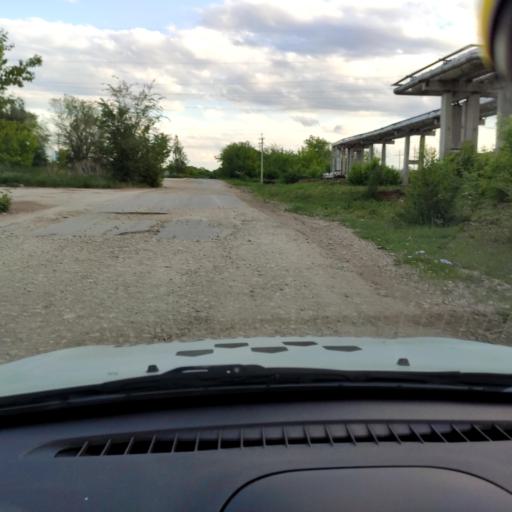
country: RU
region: Samara
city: Podstepki
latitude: 53.5808
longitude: 49.2289
